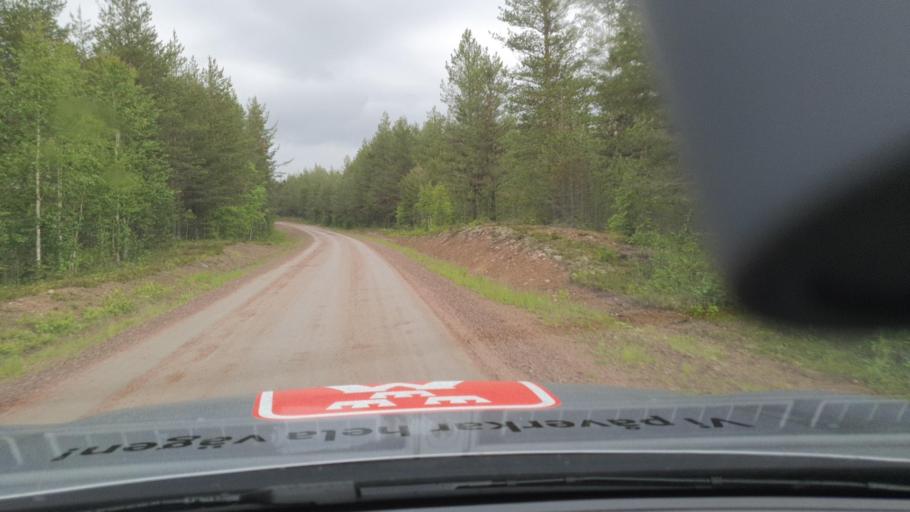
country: SE
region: Norrbotten
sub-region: Overkalix Kommun
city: OEverkalix
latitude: 66.6347
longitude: 22.7136
